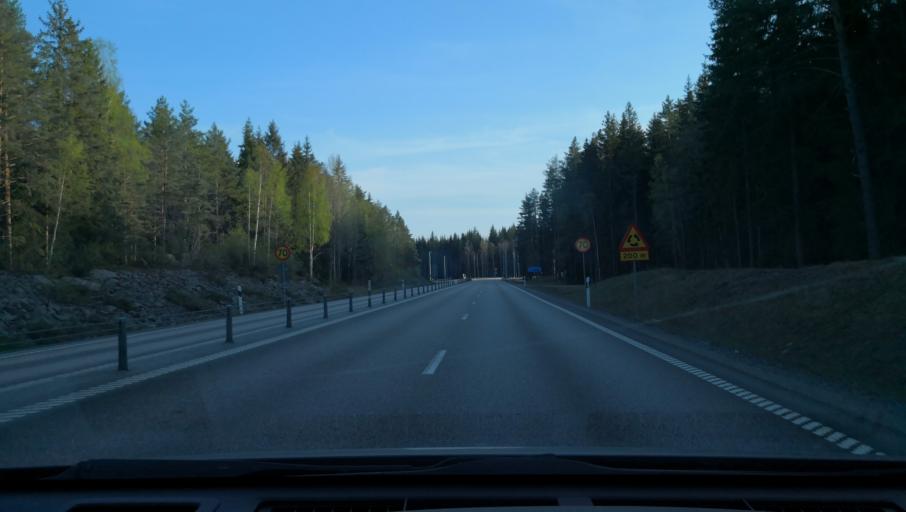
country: SE
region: Uppsala
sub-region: Heby Kommun
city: Heby
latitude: 59.9396
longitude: 16.8290
